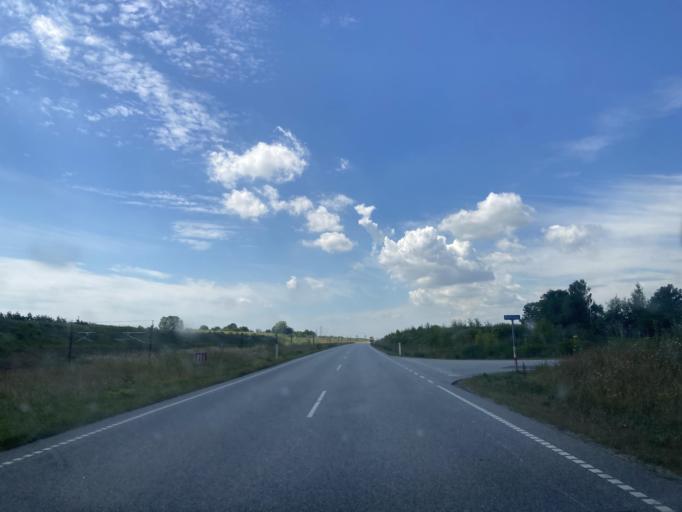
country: DK
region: Zealand
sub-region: Koge Kommune
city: Ejby
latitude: 55.4692
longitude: 12.0619
